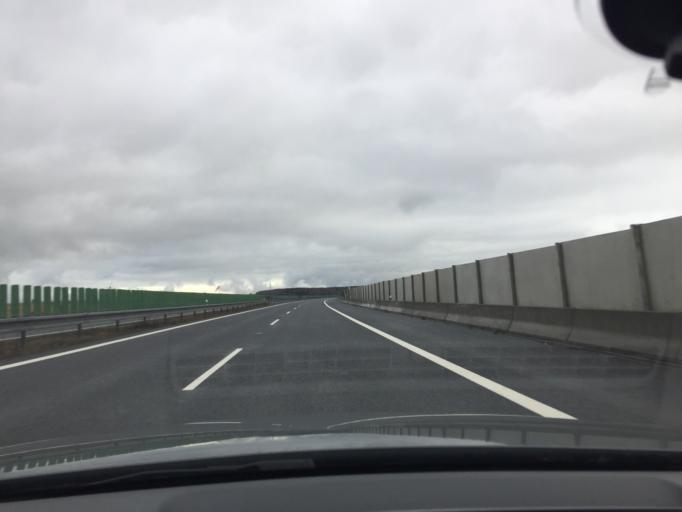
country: CZ
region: Ustecky
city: Chlumec
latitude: 50.7768
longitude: 13.9371
